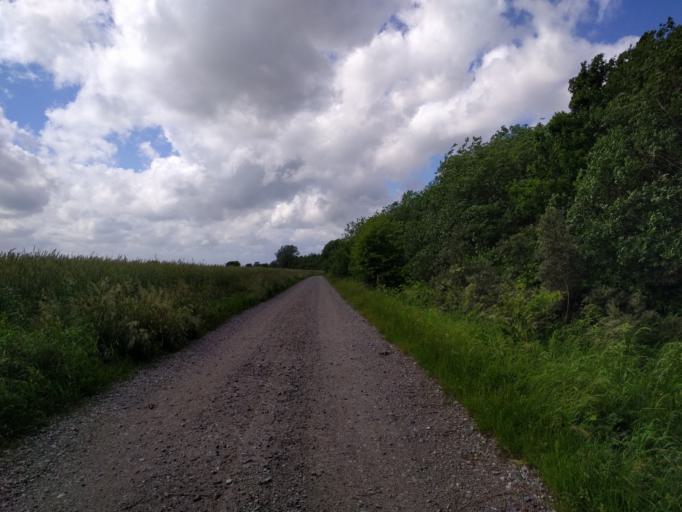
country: DK
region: South Denmark
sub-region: Kerteminde Kommune
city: Munkebo
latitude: 55.4630
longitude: 10.5176
